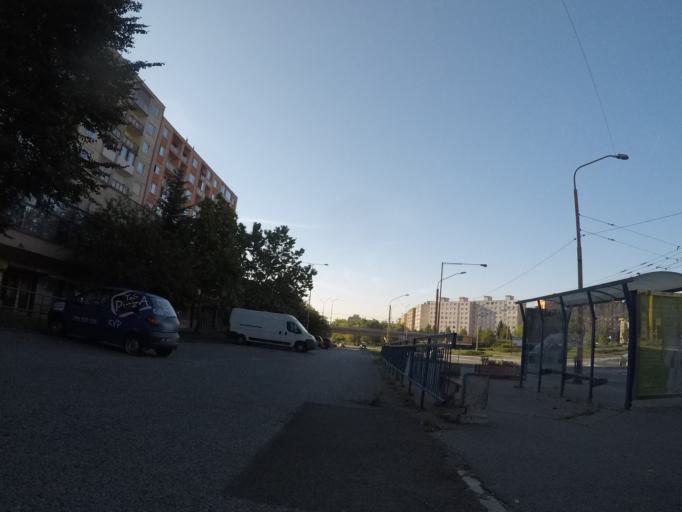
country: SK
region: Kosicky
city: Kosice
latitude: 48.7135
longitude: 21.2158
